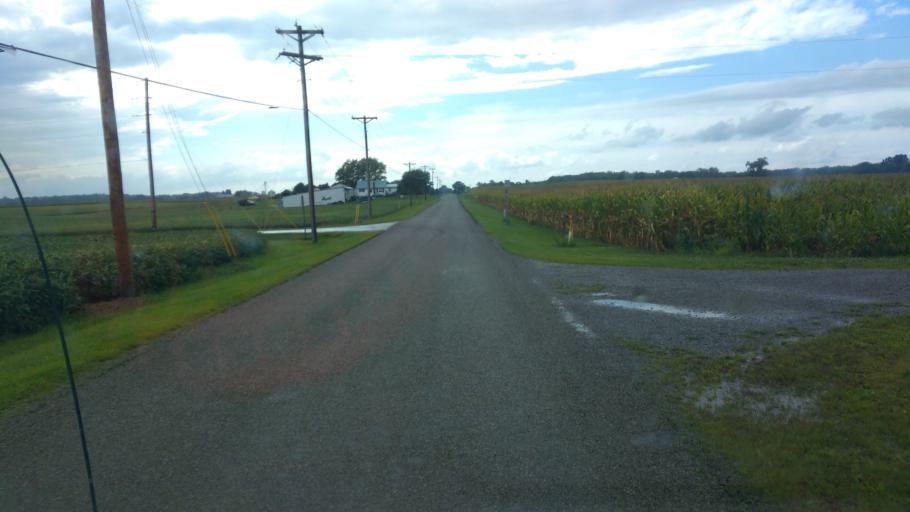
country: US
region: Ohio
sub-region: Hardin County
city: Kenton
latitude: 40.7040
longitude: -83.6380
